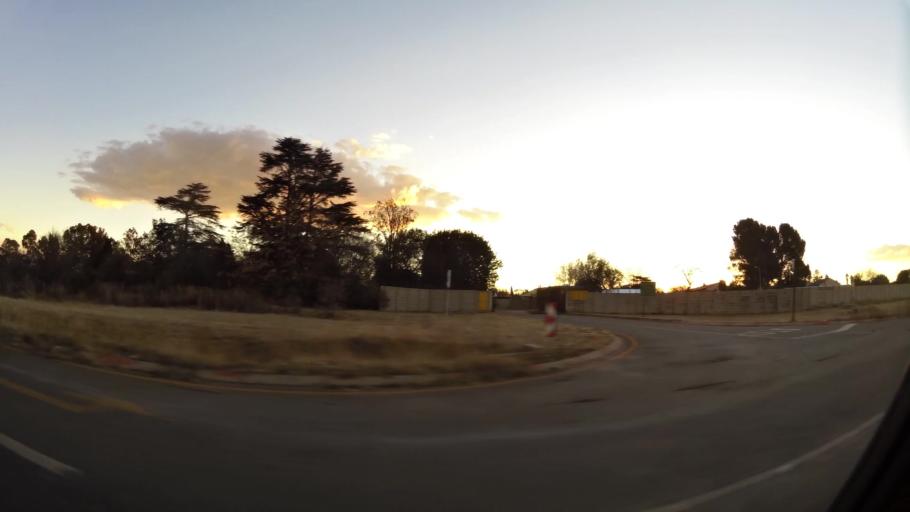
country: ZA
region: North-West
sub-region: Dr Kenneth Kaunda District Municipality
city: Potchefstroom
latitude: -26.6825
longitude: 27.0757
